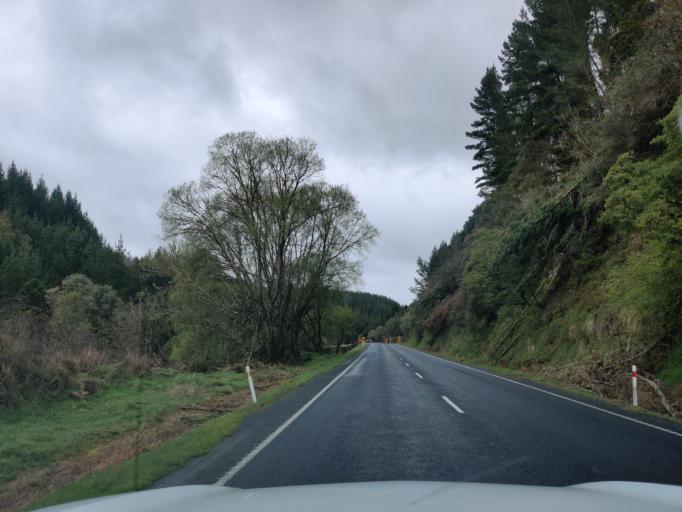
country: NZ
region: Waikato
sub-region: Otorohanga District
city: Otorohanga
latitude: -38.6546
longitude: 175.2081
